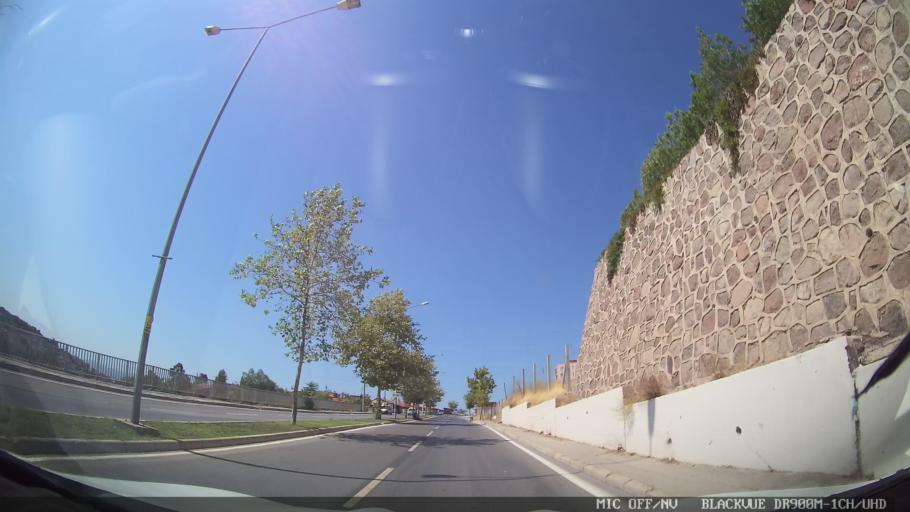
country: TR
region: Izmir
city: Karsiyaka
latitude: 38.5050
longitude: 27.0813
